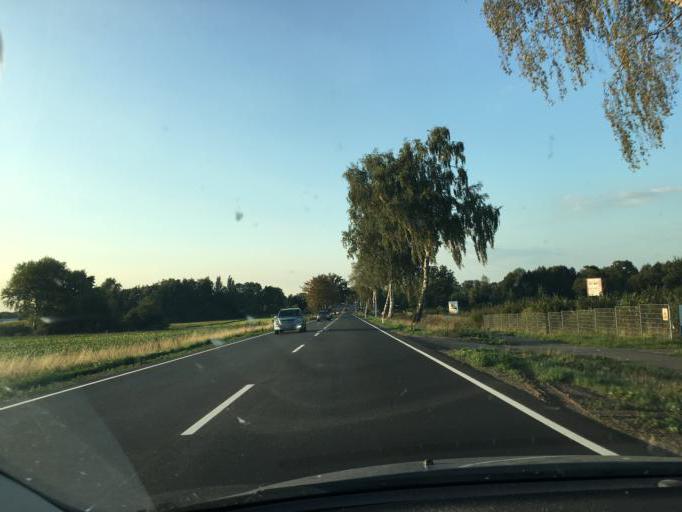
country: DE
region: Lower Saxony
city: Bergen
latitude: 52.7967
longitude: 9.9701
